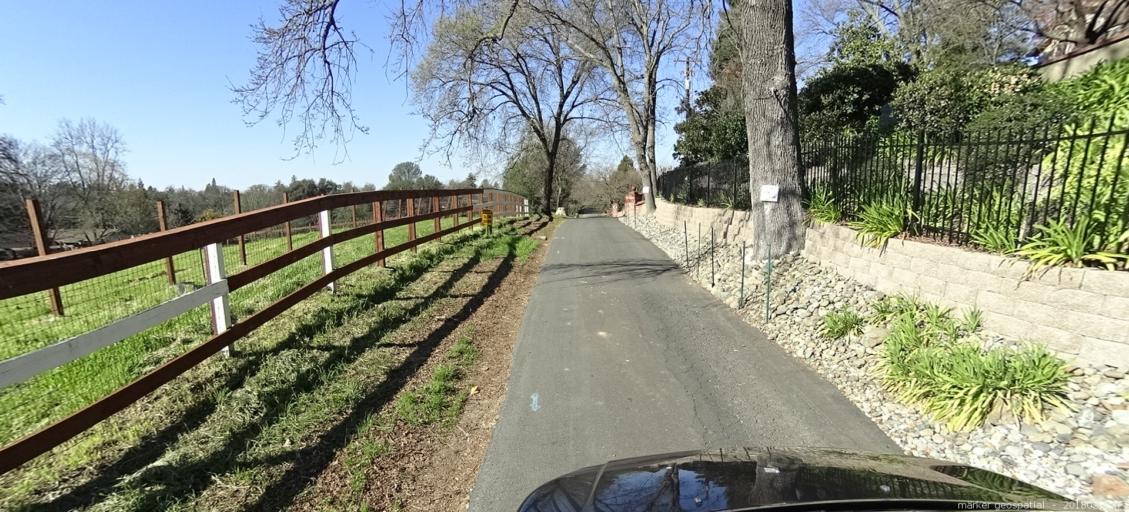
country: US
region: California
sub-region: Sacramento County
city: Orangevale
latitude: 38.7074
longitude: -121.2141
